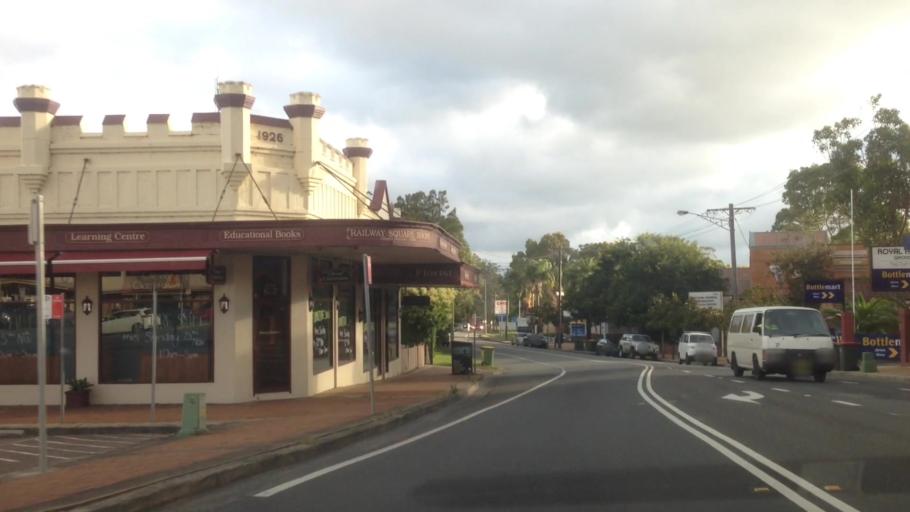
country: AU
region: New South Wales
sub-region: Wyong Shire
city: Chittaway Bay
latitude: -33.2860
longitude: 151.4245
